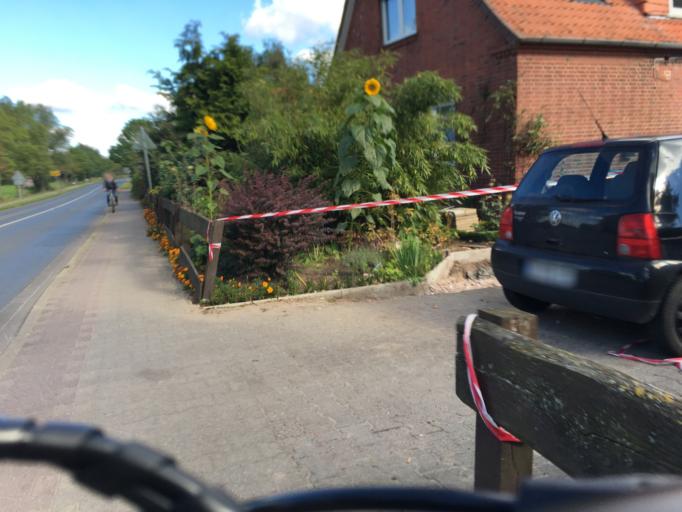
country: DE
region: Lower Saxony
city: Bardowick
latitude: 53.3008
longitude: 10.3981
